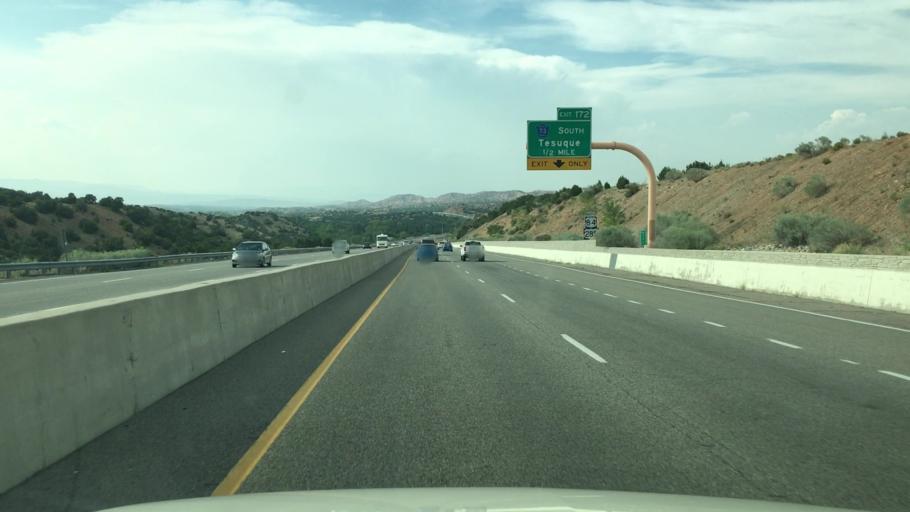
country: US
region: New Mexico
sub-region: Santa Fe County
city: Santa Fe
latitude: 35.7725
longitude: -105.9445
